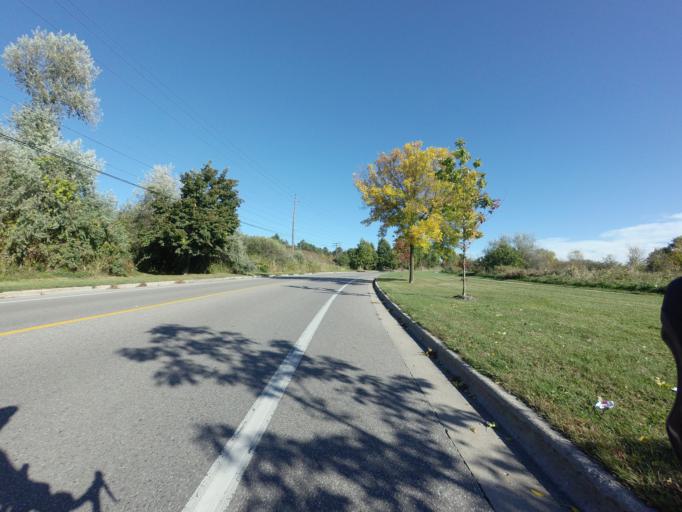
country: CA
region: Ontario
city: Oshawa
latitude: 43.8827
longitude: -78.8122
